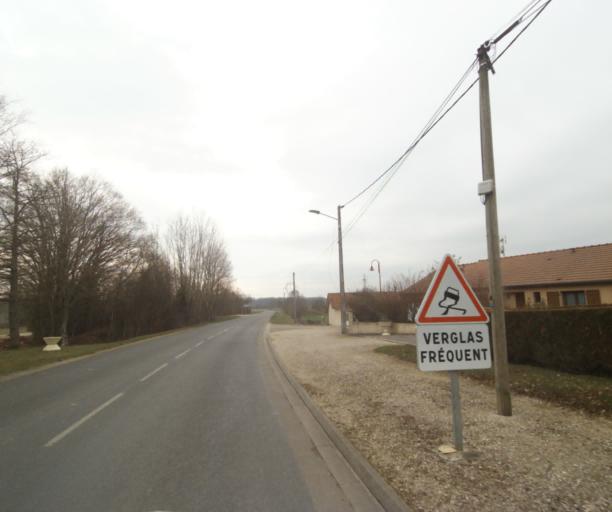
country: FR
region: Champagne-Ardenne
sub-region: Departement de la Marne
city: Pargny-sur-Saulx
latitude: 48.7467
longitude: 4.8486
